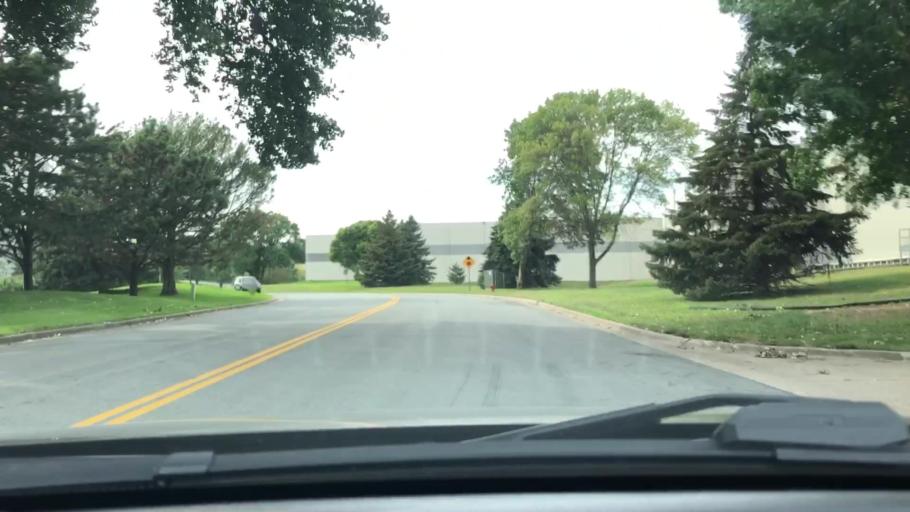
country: US
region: Minnesota
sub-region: Dakota County
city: Mendota Heights
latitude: 44.8509
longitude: -93.1565
